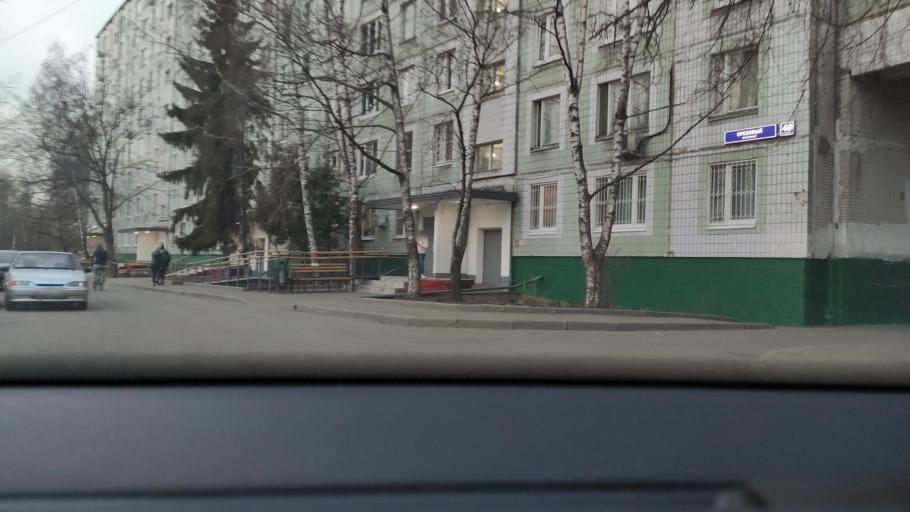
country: RU
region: Moscow
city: Zyablikovo
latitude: 55.6169
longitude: 37.7482
